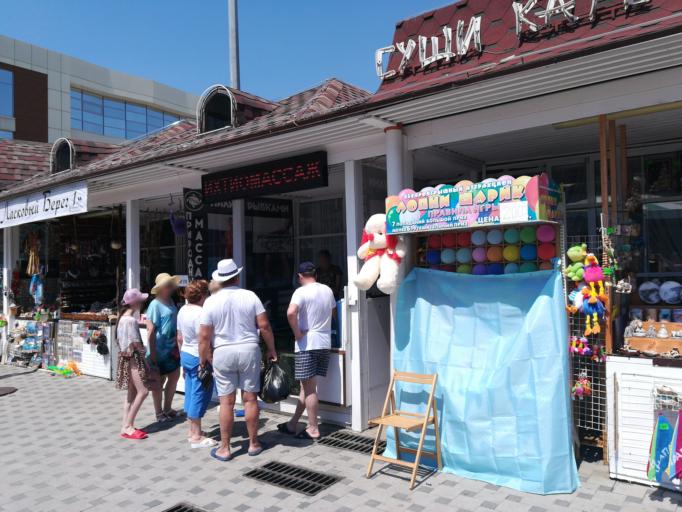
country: RU
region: Krasnodarskiy
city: Anapa
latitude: 44.8975
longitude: 37.3137
